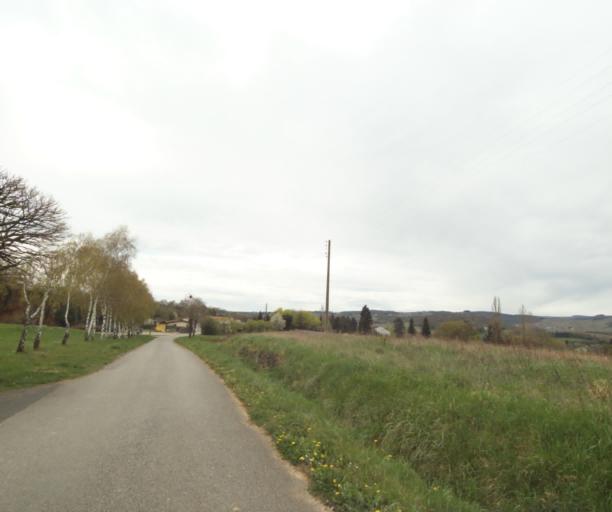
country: FR
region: Bourgogne
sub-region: Departement de Saone-et-Loire
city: Charnay-les-Macon
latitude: 46.3053
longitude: 4.7792
